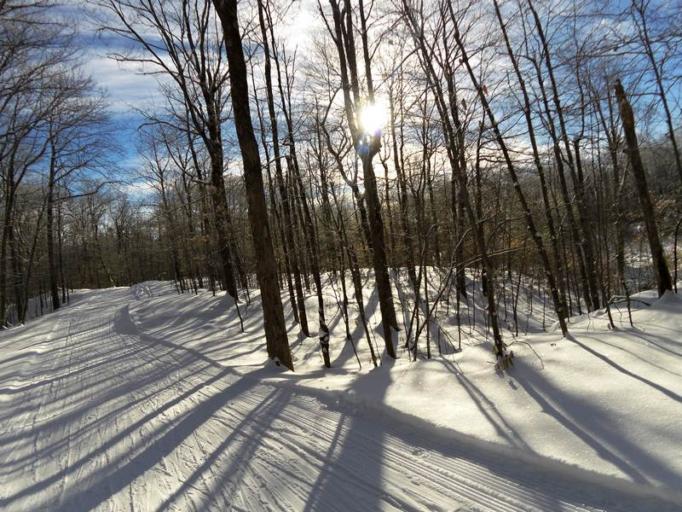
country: CA
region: Quebec
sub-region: Outaouais
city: Wakefield
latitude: 45.5089
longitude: -75.9071
